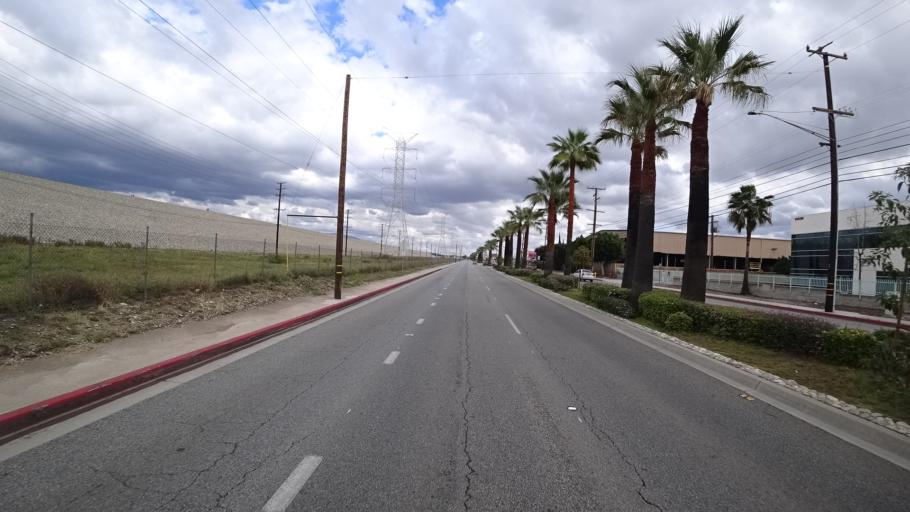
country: US
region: California
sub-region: Los Angeles County
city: Baldwin Park
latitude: 34.1070
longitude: -117.9580
